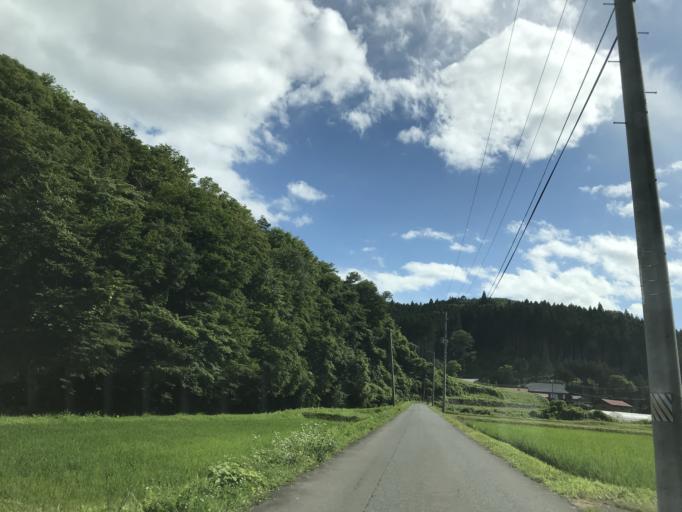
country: JP
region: Iwate
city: Ichinoseki
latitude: 38.9194
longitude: 140.9918
